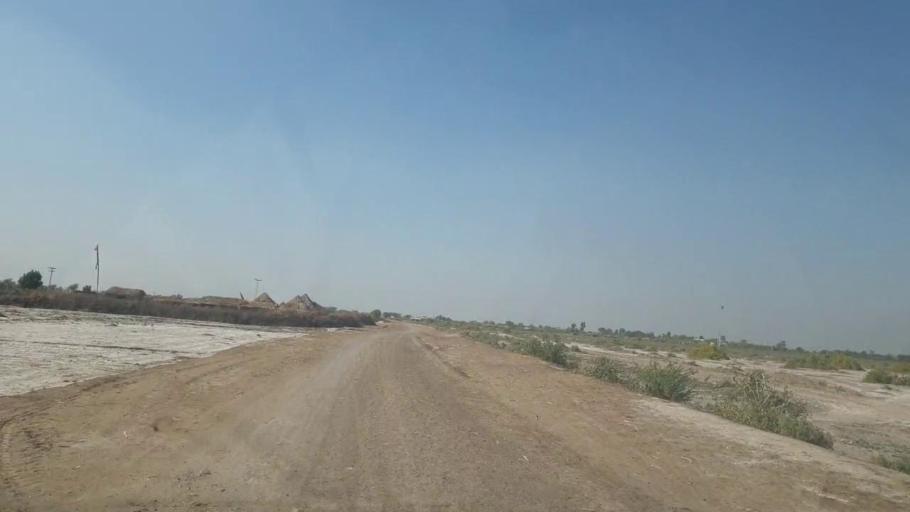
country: PK
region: Sindh
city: Mirpur Khas
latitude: 25.4747
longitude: 69.1225
